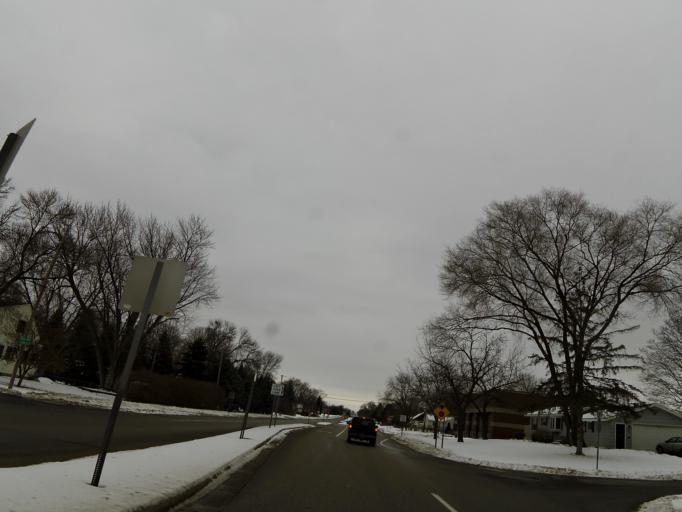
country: US
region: Minnesota
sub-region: Dakota County
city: Inver Grove Heights
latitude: 44.8481
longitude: -93.0363
